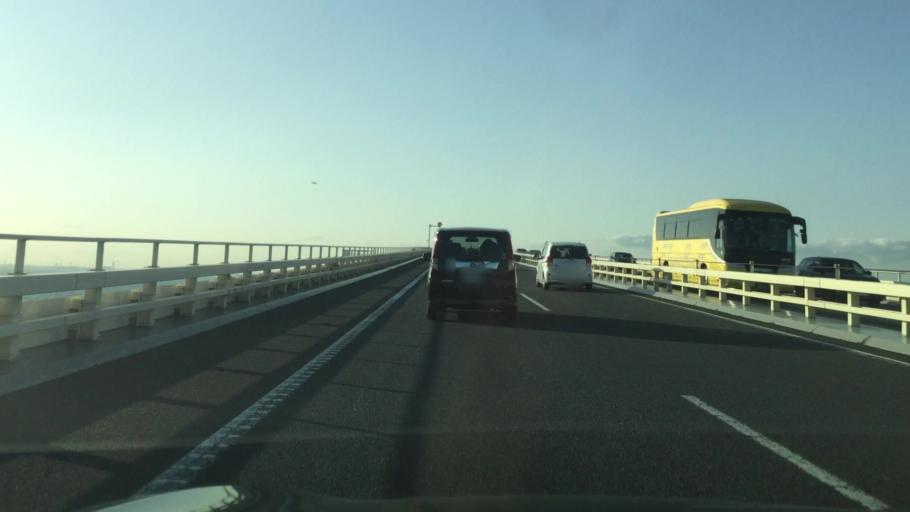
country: JP
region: Chiba
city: Kisarazu
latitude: 35.4519
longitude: 139.8925
